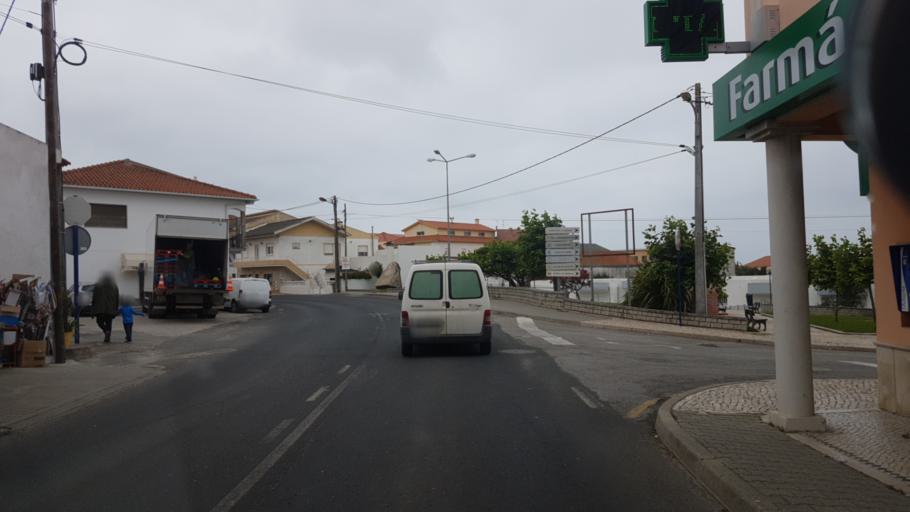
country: PT
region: Lisbon
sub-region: Lourinha
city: Lourinha
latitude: 39.2020
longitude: -9.3303
